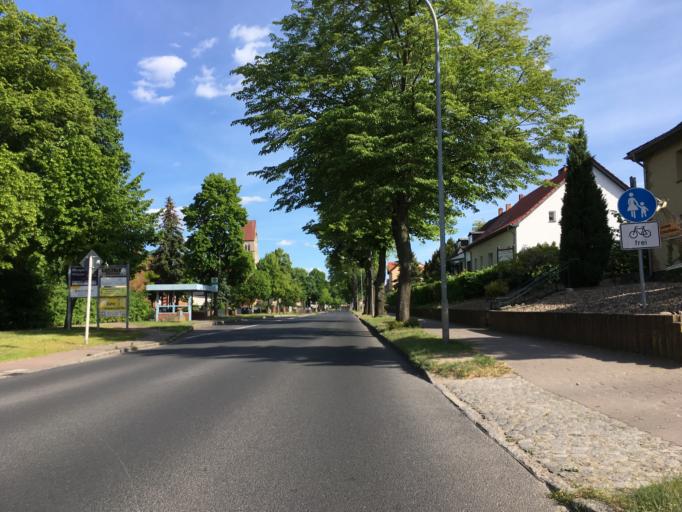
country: DE
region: Brandenburg
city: Wriezen
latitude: 52.7251
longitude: 14.1276
